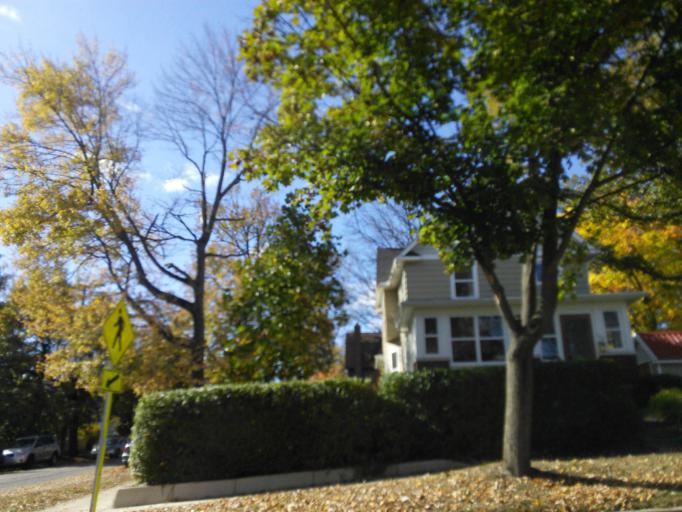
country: US
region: Michigan
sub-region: Washtenaw County
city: Ann Arbor
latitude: 42.2809
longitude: -83.7586
